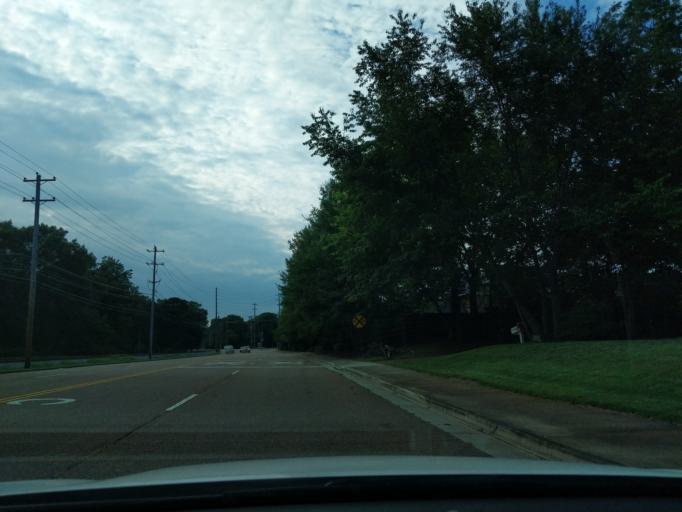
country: US
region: Tennessee
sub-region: Shelby County
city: Germantown
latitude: 35.0790
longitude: -89.8001
